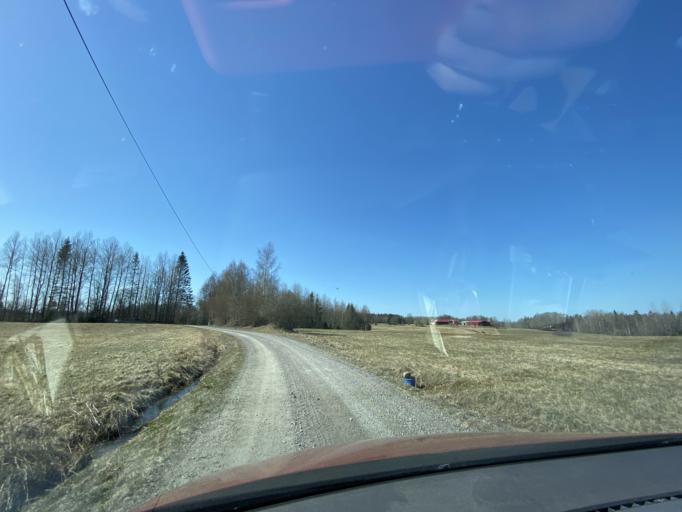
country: SE
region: Soedermanland
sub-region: Vingakers Kommun
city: Vingaker
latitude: 59.0275
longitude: 15.7573
